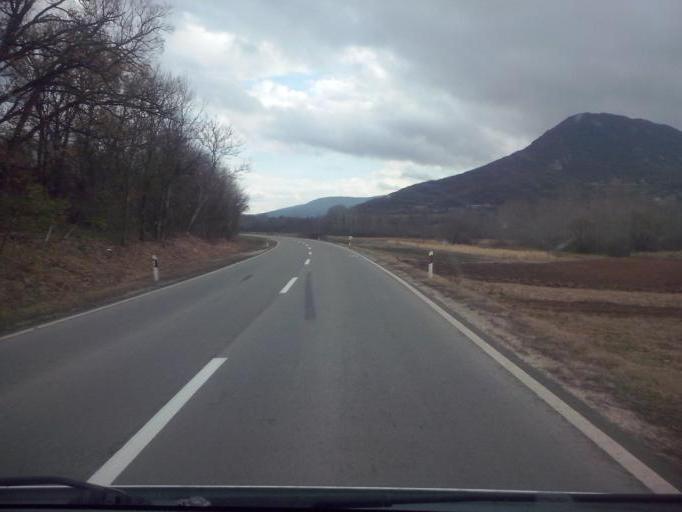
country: RS
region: Central Serbia
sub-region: Pomoravski Okrug
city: Paracin
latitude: 43.8607
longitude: 21.5188
